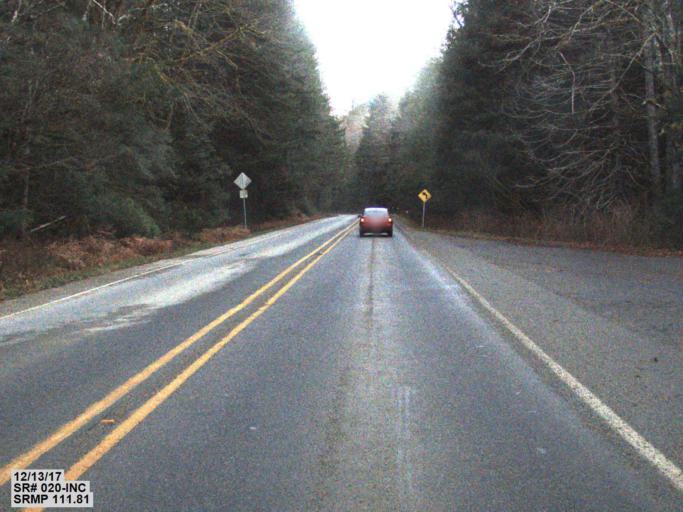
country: US
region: Washington
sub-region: Snohomish County
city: Darrington
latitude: 48.5930
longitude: -121.3745
